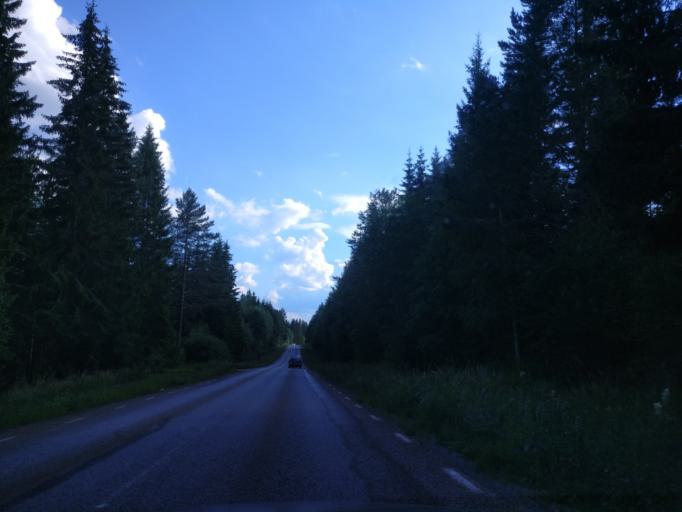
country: SE
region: Dalarna
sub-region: Ludvika Kommun
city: Ludvika
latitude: 60.2756
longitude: 15.0755
